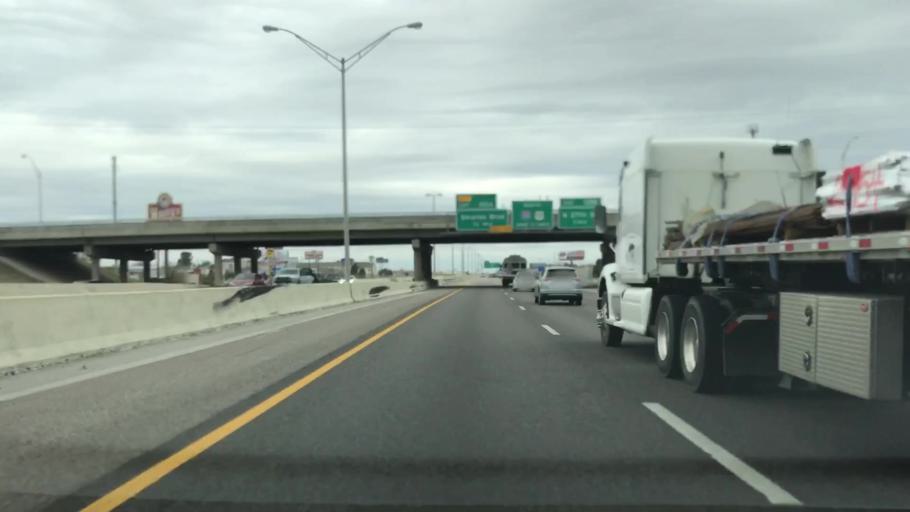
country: US
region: Oklahoma
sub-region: Cleveland County
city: Moore
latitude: 35.3481
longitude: -97.4946
